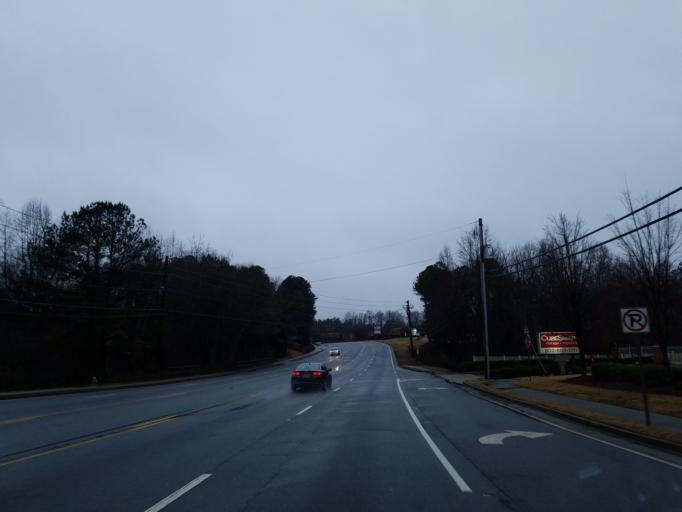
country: US
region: Georgia
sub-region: Gwinnett County
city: Norcross
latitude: 33.9613
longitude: -84.2491
